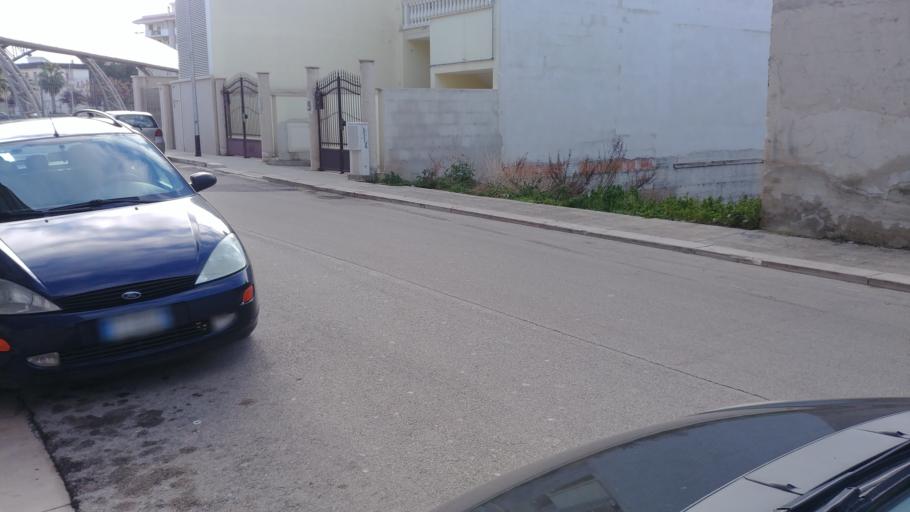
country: IT
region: Apulia
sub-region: Provincia di Barletta - Andria - Trani
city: Andria
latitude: 41.2389
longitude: 16.2955
